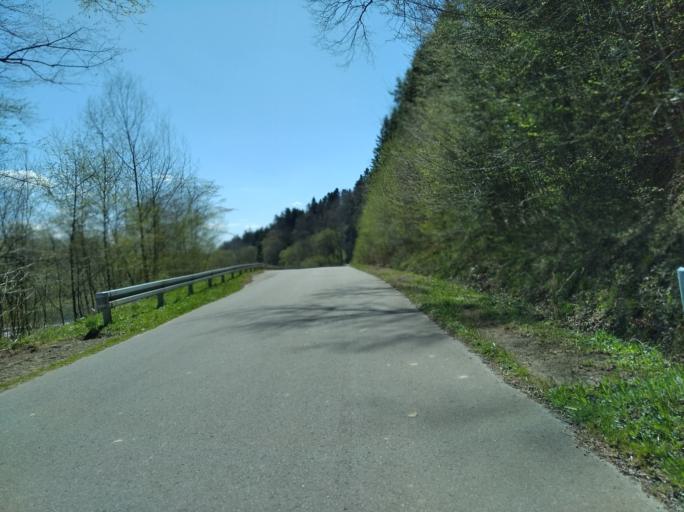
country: PL
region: Subcarpathian Voivodeship
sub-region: Powiat brzozowski
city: Dydnia
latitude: 49.6869
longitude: 22.2374
